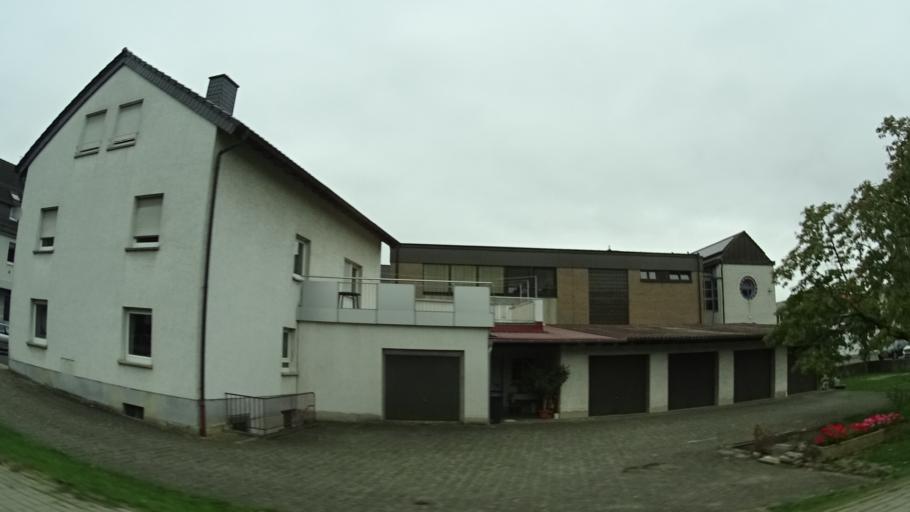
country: DE
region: Hesse
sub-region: Regierungsbezirk Kassel
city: Flieden
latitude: 50.4225
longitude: 9.5704
